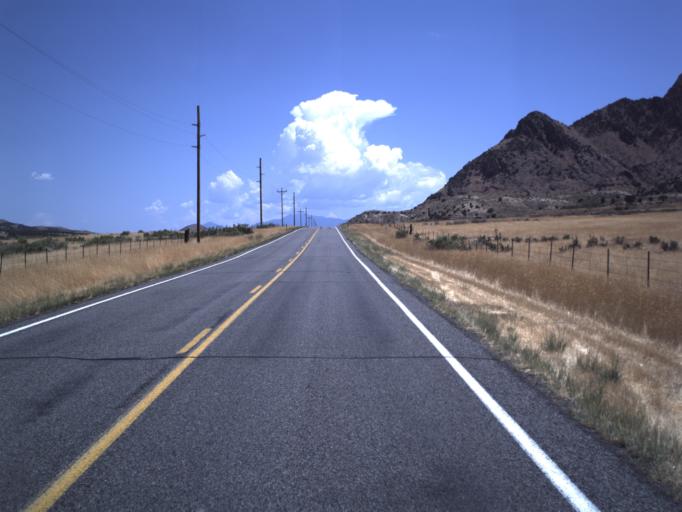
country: US
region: Utah
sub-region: Millard County
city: Delta
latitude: 39.5447
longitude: -112.2346
